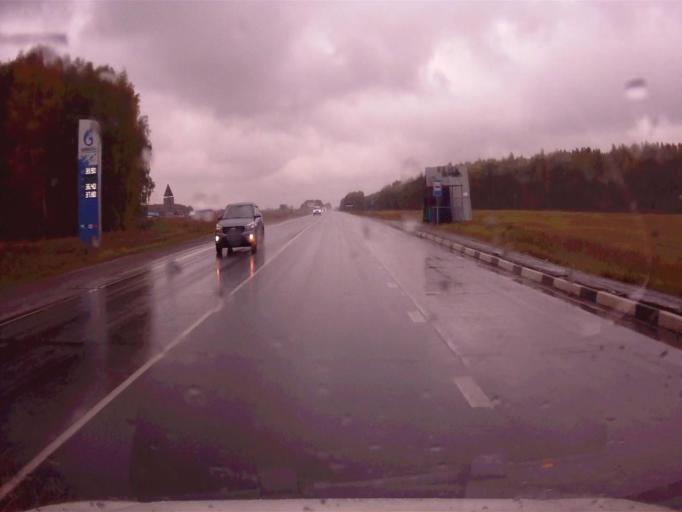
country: RU
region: Chelyabinsk
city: Argayash
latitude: 55.4182
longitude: 61.0229
